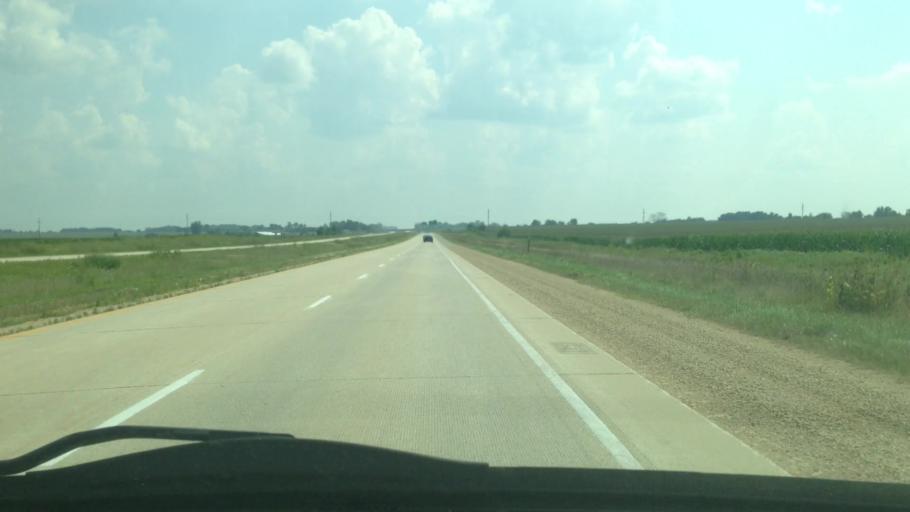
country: US
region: Iowa
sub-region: Chickasaw County
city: New Hampton
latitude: 42.9776
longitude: -92.3179
